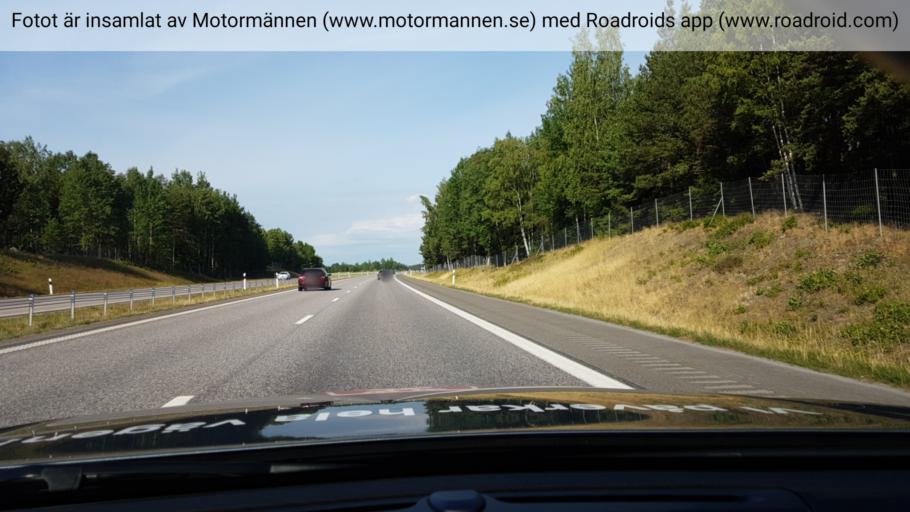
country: SE
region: OEstergoetland
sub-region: Linkopings Kommun
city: Linghem
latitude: 58.4530
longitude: 15.7636
